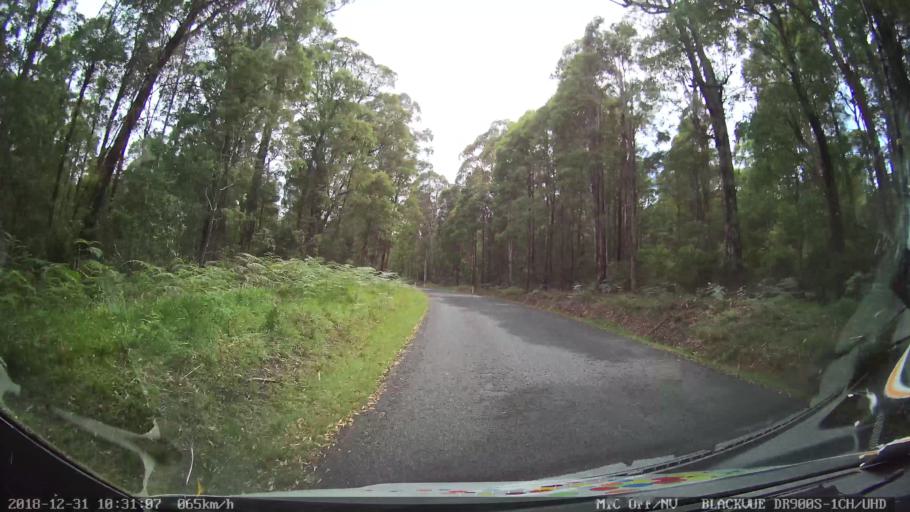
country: AU
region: New South Wales
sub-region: Snowy River
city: Jindabyne
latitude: -36.4597
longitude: 148.1550
